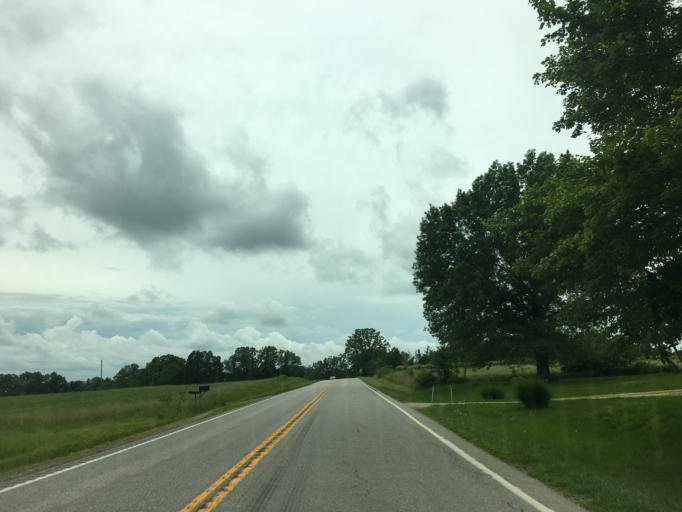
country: US
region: Missouri
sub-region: Gasconade County
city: Owensville
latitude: 38.4751
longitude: -91.4631
